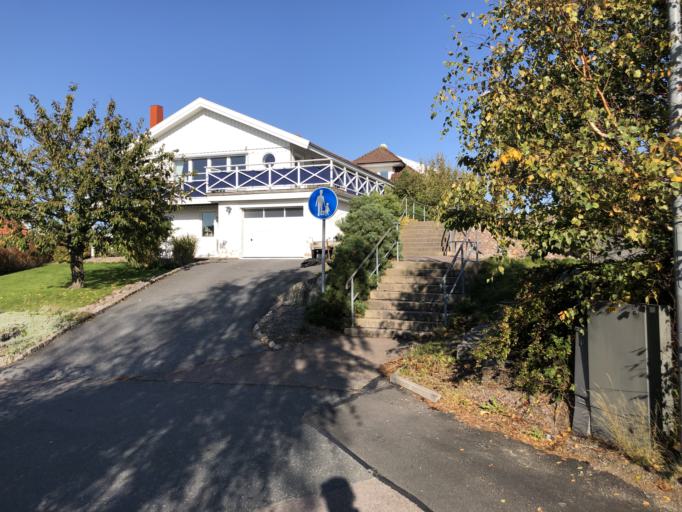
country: SE
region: Vaestra Goetaland
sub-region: Goteborg
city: Billdal
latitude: 57.6222
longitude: 11.8912
